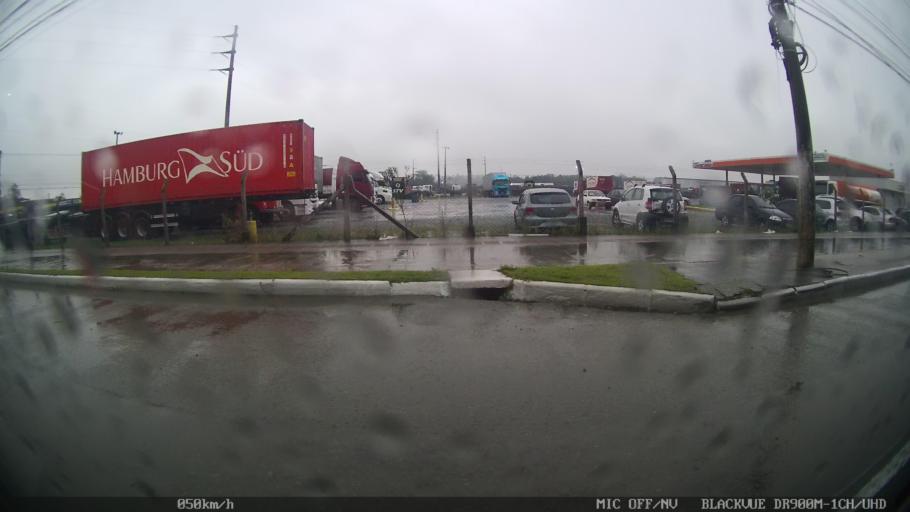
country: BR
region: Santa Catarina
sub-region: Itajai
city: Itajai
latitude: -26.8911
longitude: -48.7138
